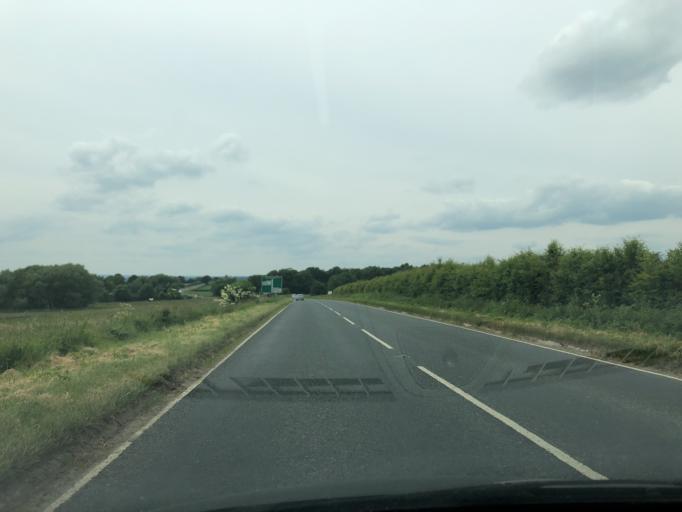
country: GB
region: England
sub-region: North Yorkshire
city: Great Habton
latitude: 54.2637
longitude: -0.8878
